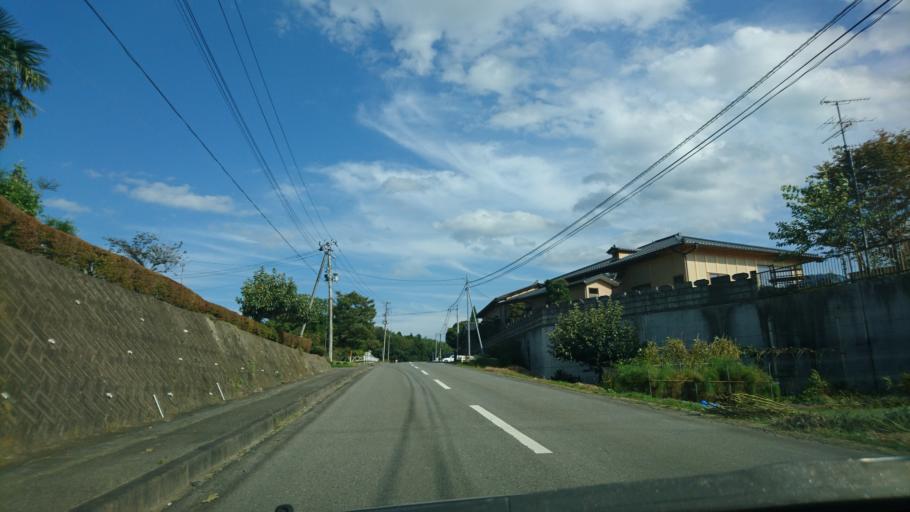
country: JP
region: Iwate
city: Ichinoseki
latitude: 38.8433
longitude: 141.1846
